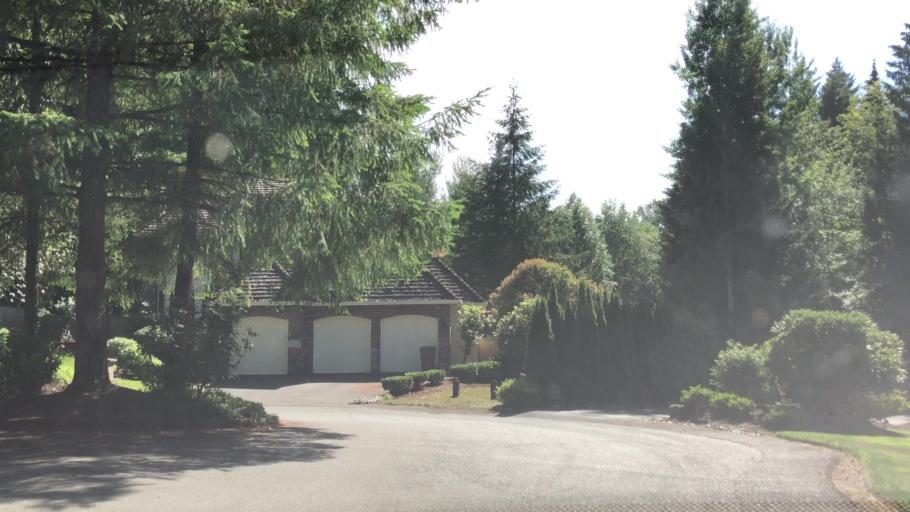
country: US
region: Washington
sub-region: King County
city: Cottage Lake
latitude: 47.7068
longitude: -122.0754
